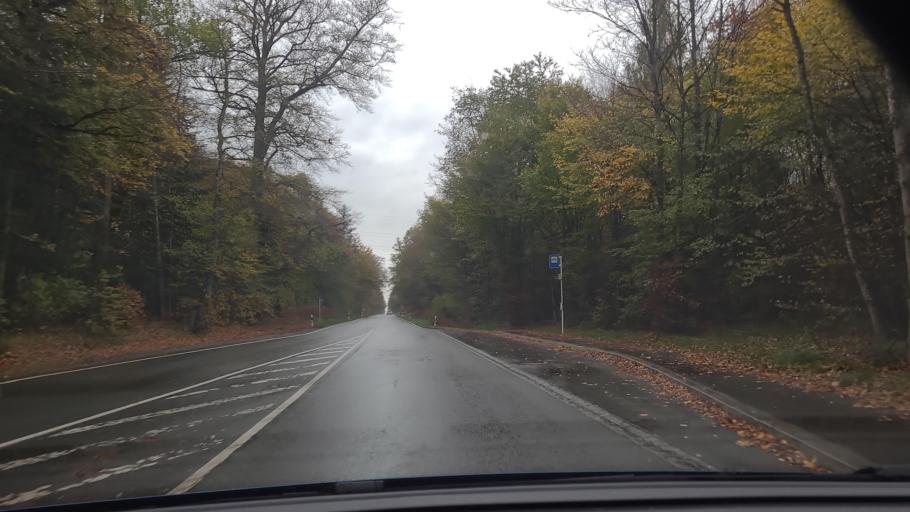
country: LU
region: Luxembourg
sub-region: Canton de Luxembourg
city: Luxembourg
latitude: 49.6321
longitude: 6.1105
